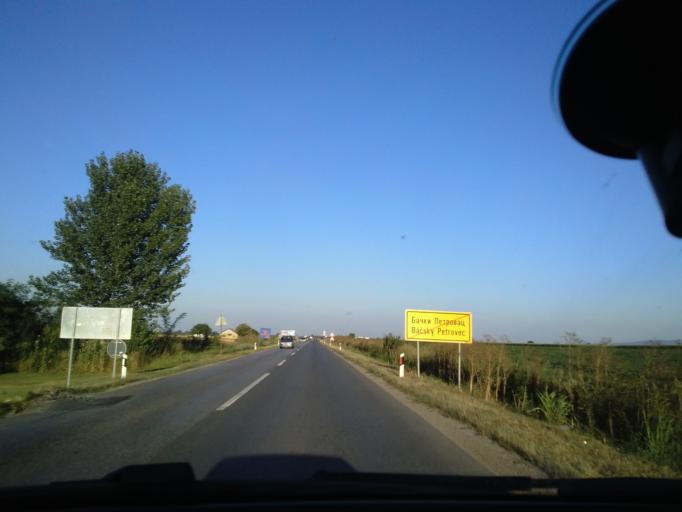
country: RS
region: Autonomna Pokrajina Vojvodina
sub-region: Juznobacki Okrug
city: Backi Petrovac
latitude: 45.3490
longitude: 19.6185
